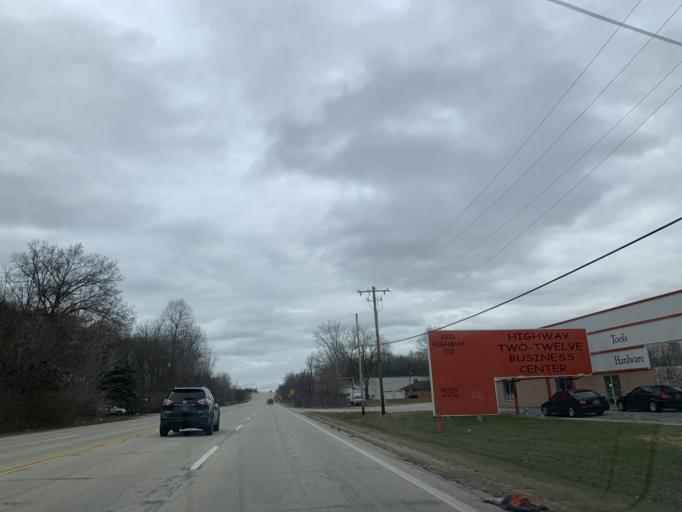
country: US
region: Indiana
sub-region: LaPorte County
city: Trail Creek
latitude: 41.7102
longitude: -86.8259
